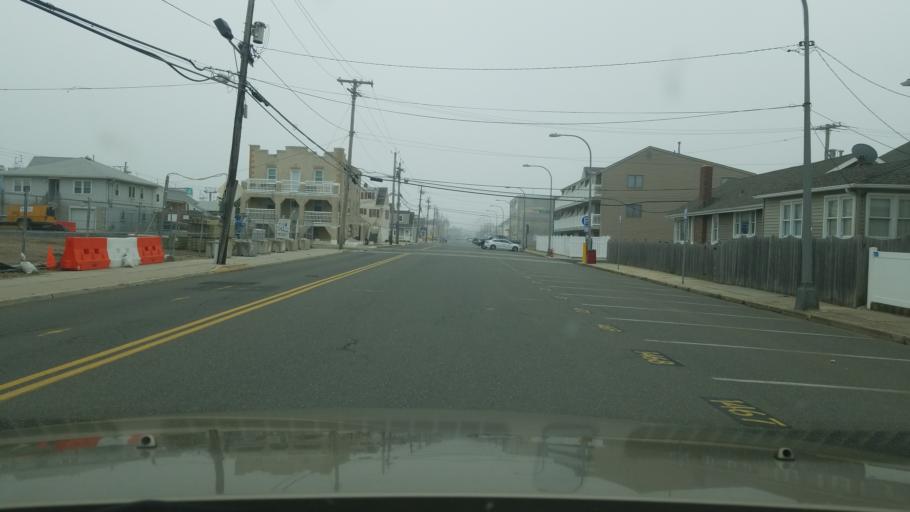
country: US
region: New Jersey
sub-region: Ocean County
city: Seaside Heights
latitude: 39.9471
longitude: -74.0702
